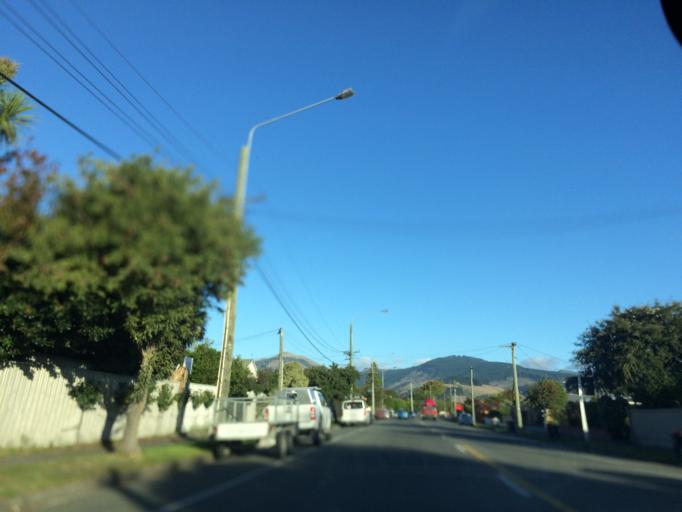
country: NZ
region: Canterbury
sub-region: Christchurch City
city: Christchurch
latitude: -43.5648
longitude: 172.6092
